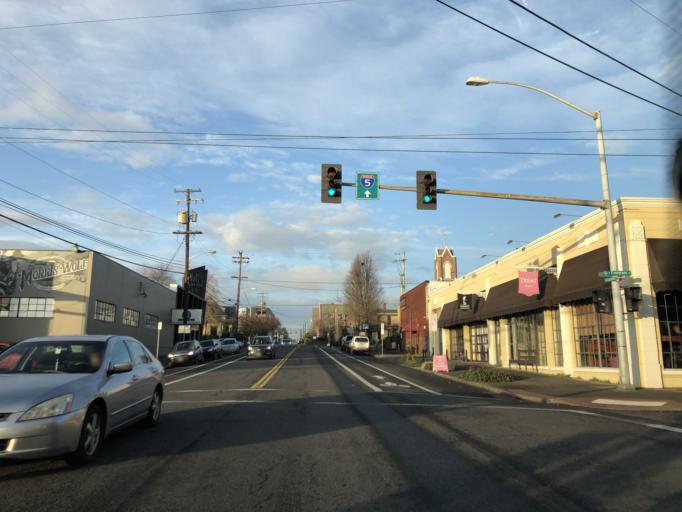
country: US
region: Washington
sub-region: Clark County
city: Vancouver
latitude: 45.6287
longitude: -122.6738
